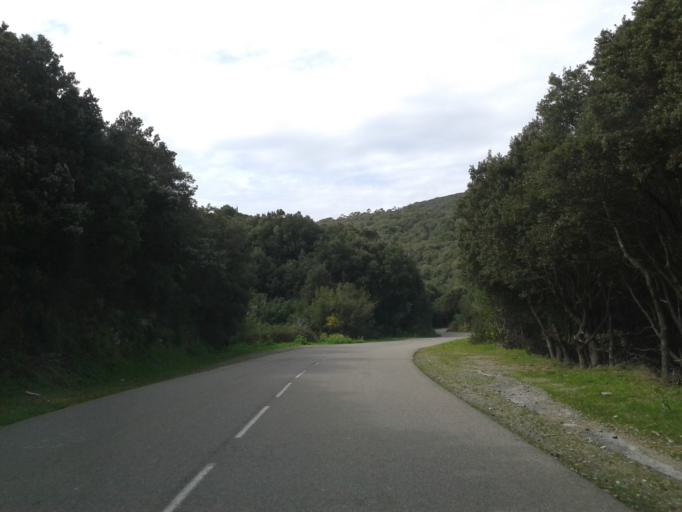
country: FR
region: Corsica
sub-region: Departement de la Haute-Corse
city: Brando
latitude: 42.9429
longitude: 9.4636
